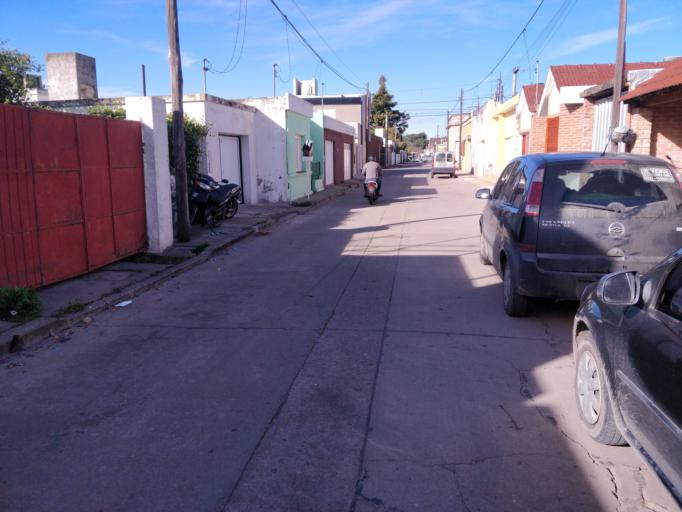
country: AR
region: Cordoba
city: Leones
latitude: -32.6633
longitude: -62.2981
